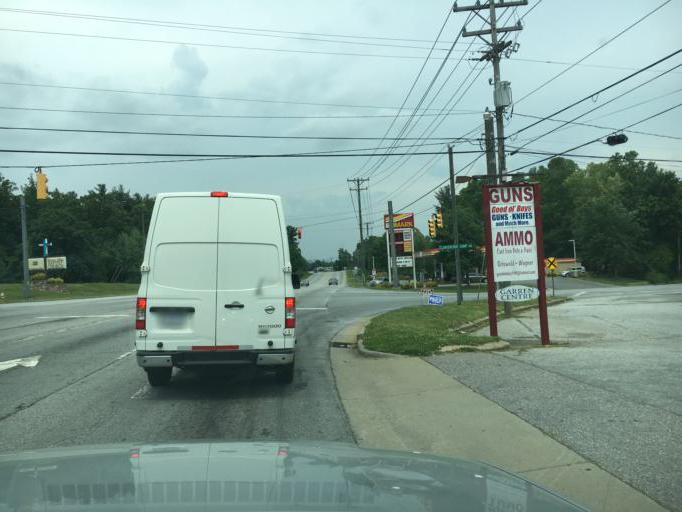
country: US
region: North Carolina
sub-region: Henderson County
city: Mountain Home
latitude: 35.3611
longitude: -82.4807
